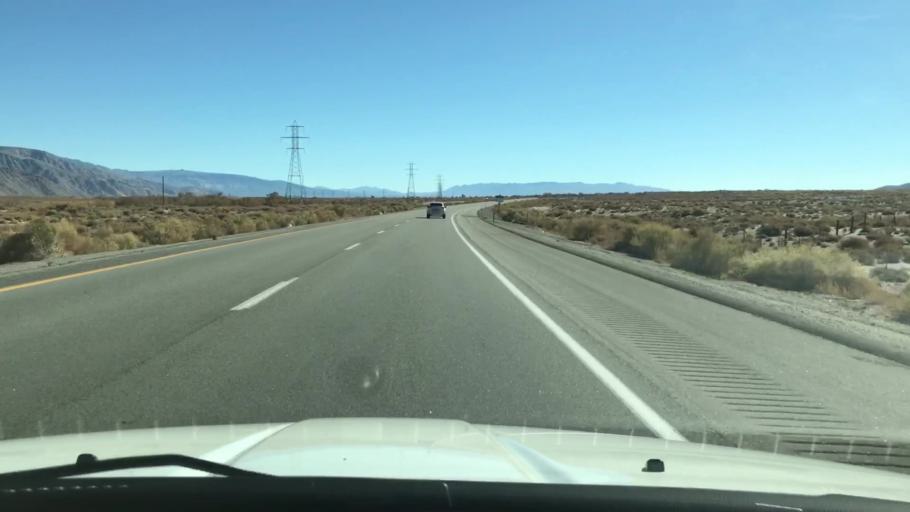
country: US
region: California
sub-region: Inyo County
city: Lone Pine
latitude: 36.6434
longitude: -118.0844
